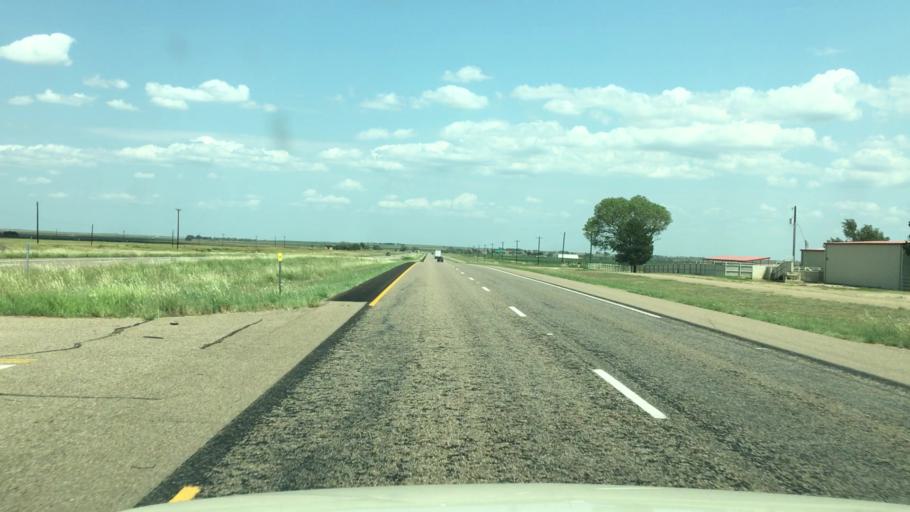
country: US
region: Texas
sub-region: Donley County
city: Clarendon
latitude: 35.0315
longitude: -101.1179
